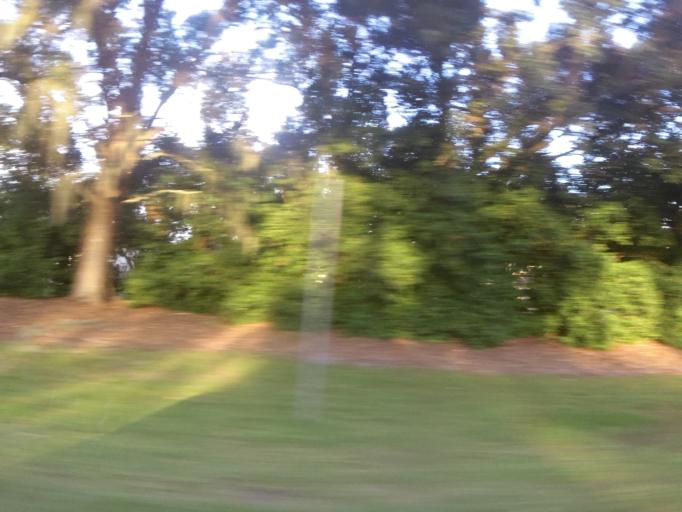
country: US
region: Florida
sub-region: Saint Johns County
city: Palm Valley
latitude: 30.1600
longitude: -81.3846
